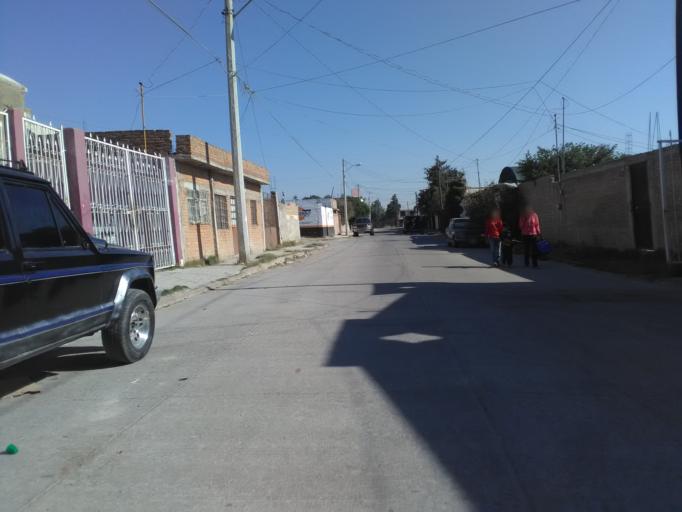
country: MX
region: Durango
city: Victoria de Durango
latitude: 24.0120
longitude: -104.6391
